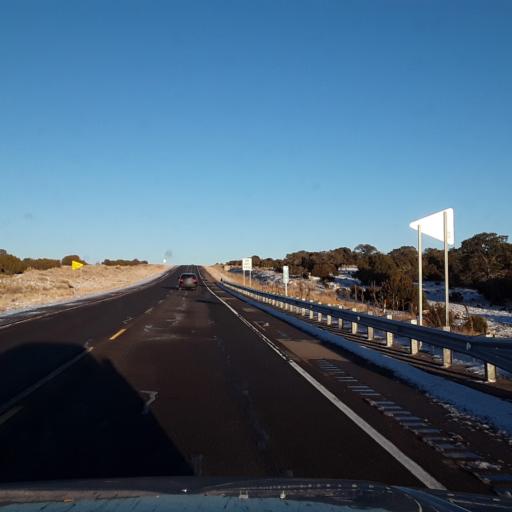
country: US
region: New Mexico
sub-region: Lincoln County
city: Carrizozo
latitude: 34.2333
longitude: -105.6211
